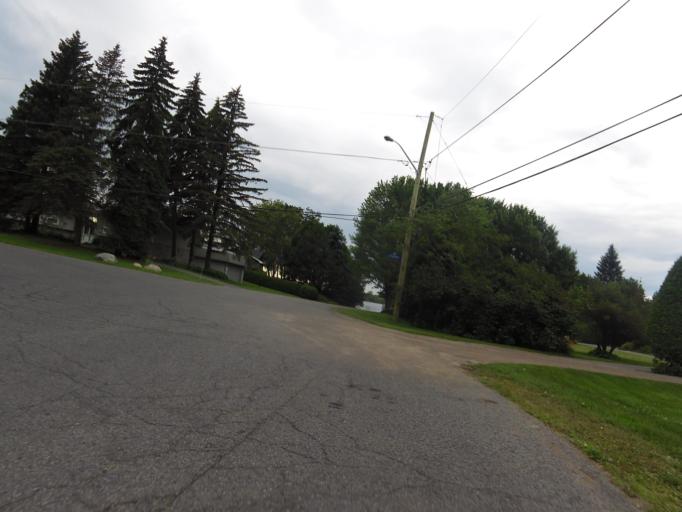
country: CA
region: Ontario
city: Bells Corners
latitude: 45.3637
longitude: -75.8646
